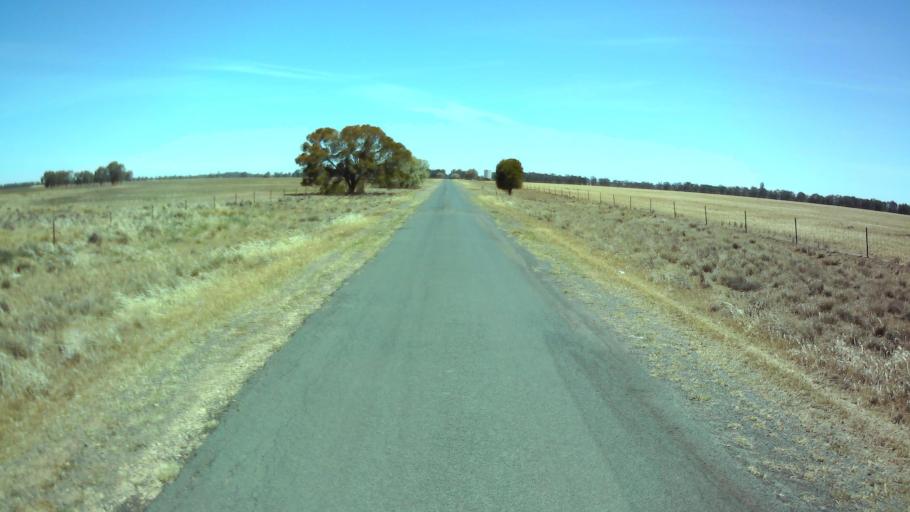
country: AU
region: New South Wales
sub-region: Weddin
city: Grenfell
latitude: -33.8550
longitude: 147.6950
